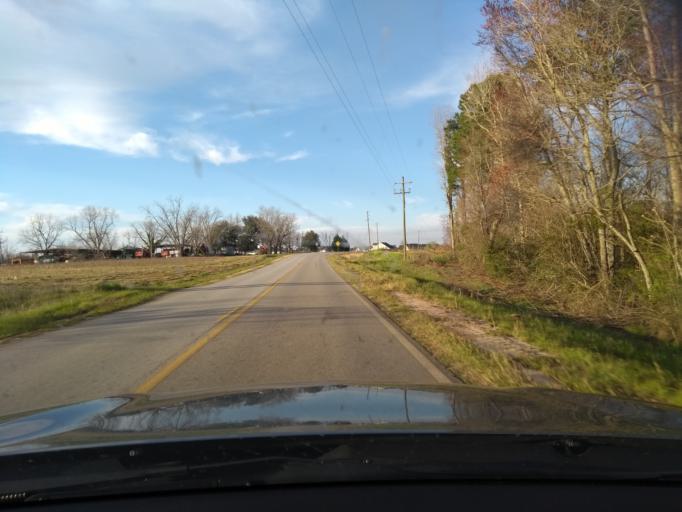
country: US
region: Georgia
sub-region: Bulloch County
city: Statesboro
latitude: 32.3569
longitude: -81.7712
